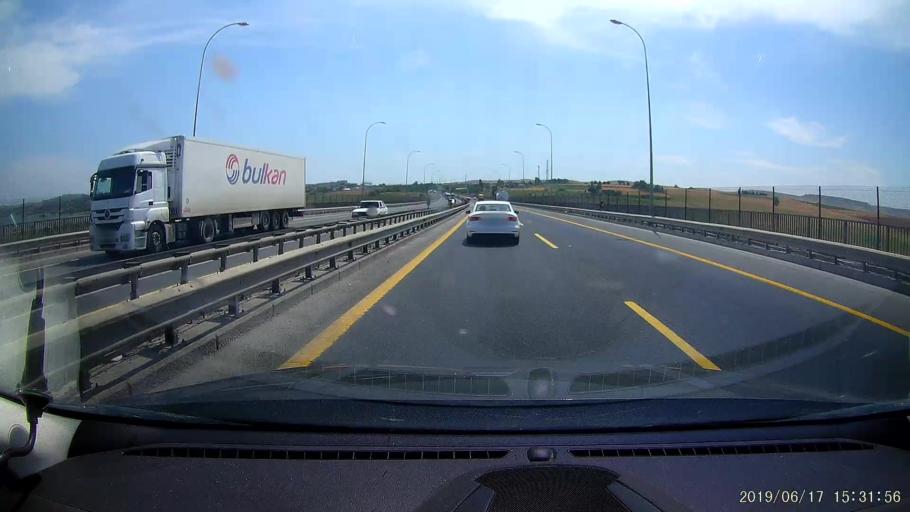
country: TR
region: Istanbul
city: Muratbey
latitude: 41.1019
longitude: 28.5221
